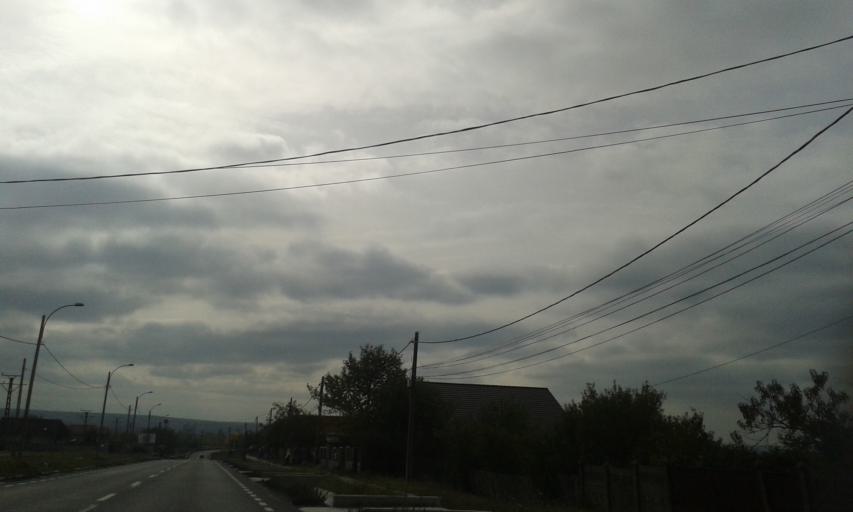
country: RO
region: Gorj
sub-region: Comuna Bumbesti-Jiu
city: Bumbesti-Jiu
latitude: 45.1715
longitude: 23.3813
